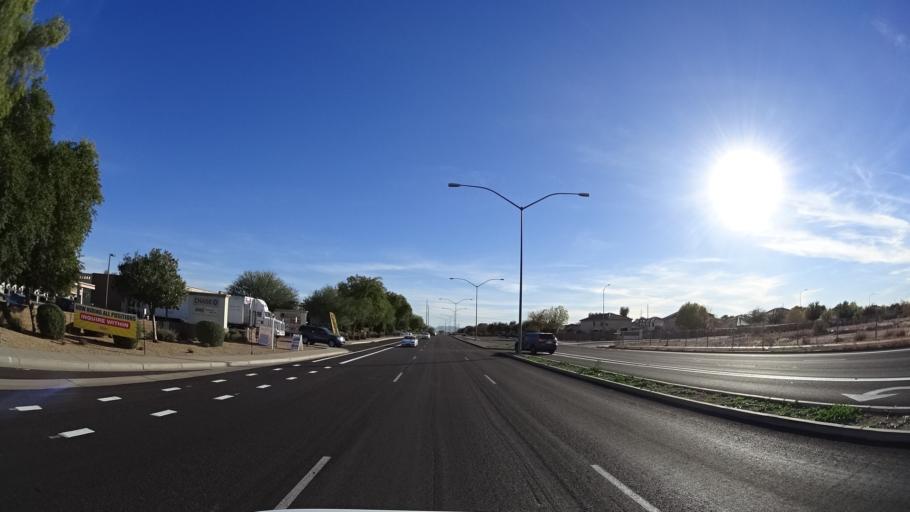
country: US
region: Arizona
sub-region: Pinal County
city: Apache Junction
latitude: 33.3632
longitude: -111.6359
